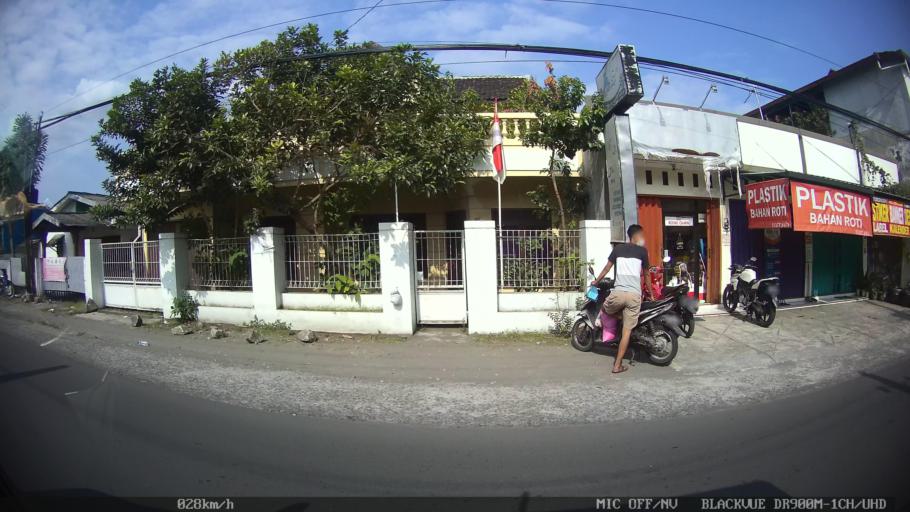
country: ID
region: Daerah Istimewa Yogyakarta
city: Depok
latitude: -7.7515
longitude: 110.4487
